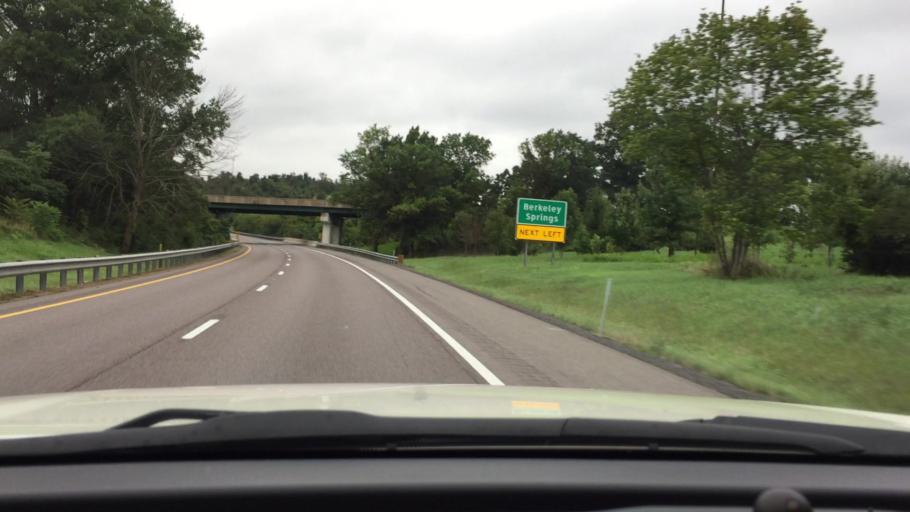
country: US
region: Maryland
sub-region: Washington County
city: Hancock
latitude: 39.7154
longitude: -78.1885
